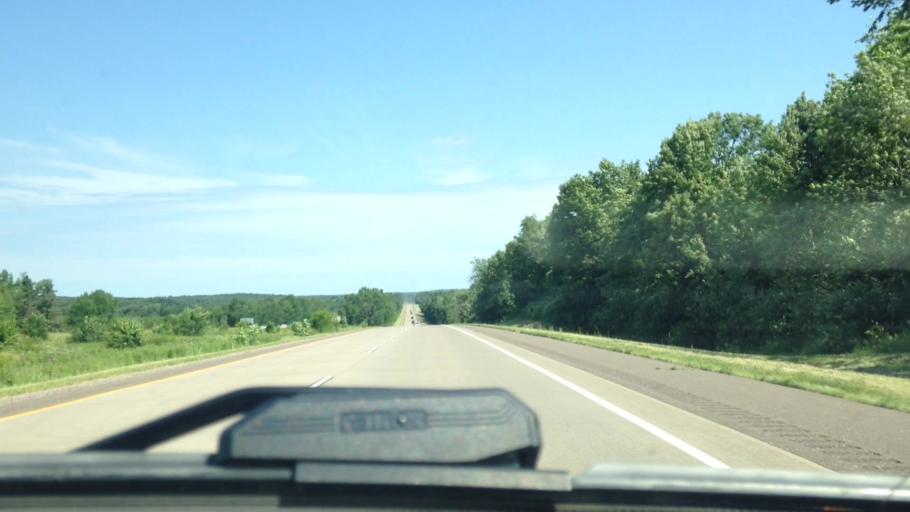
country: US
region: Wisconsin
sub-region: Barron County
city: Rice Lake
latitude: 45.5364
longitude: -91.7605
